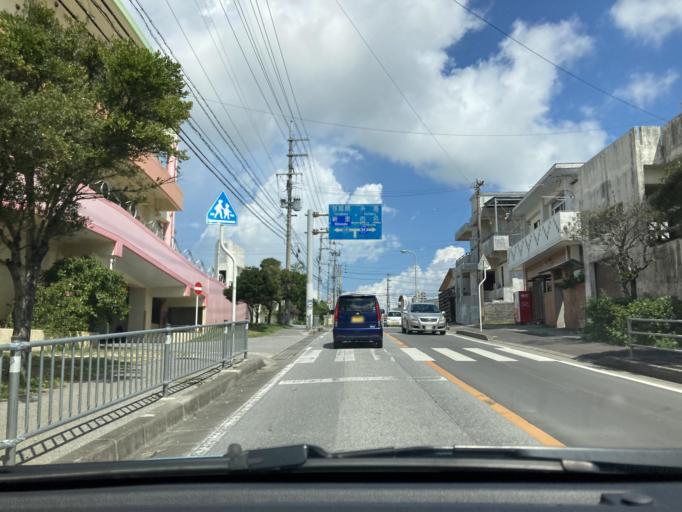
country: JP
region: Okinawa
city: Tomigusuku
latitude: 26.1544
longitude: 127.7806
